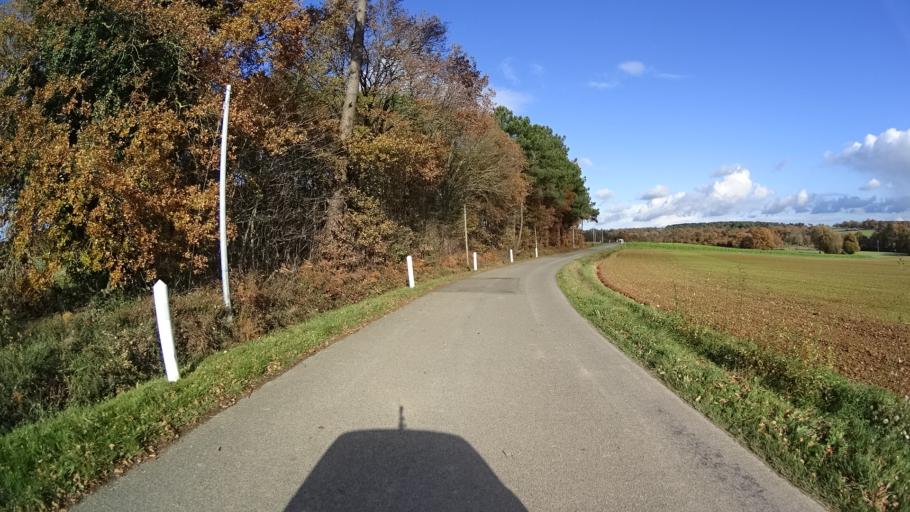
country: FR
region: Brittany
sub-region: Departement du Morbihan
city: Carentoir
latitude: 47.8410
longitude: -2.1538
